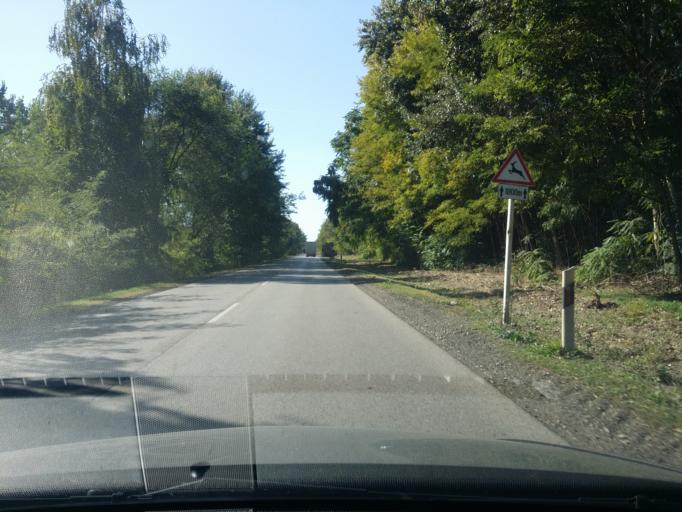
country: HU
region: Bacs-Kiskun
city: Lakitelek
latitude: 46.8740
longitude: 19.9738
